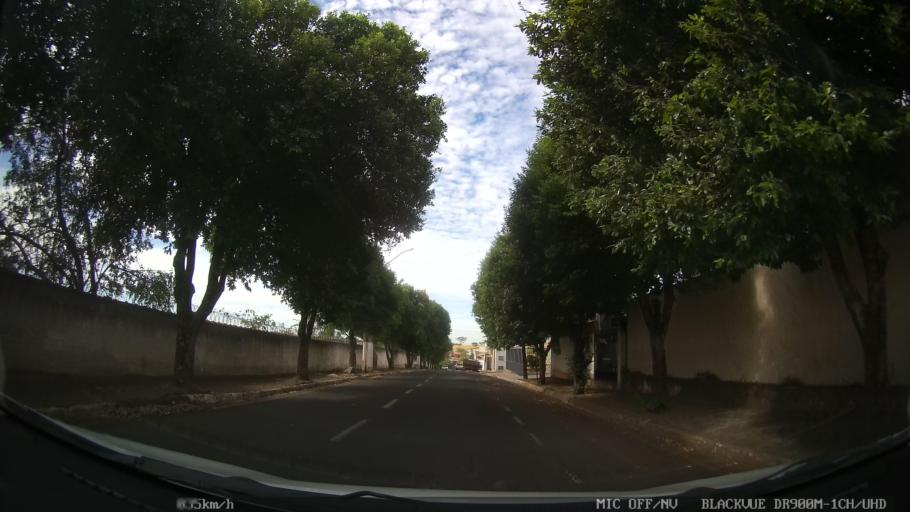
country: BR
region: Sao Paulo
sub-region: Catanduva
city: Catanduva
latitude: -21.1500
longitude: -48.9668
